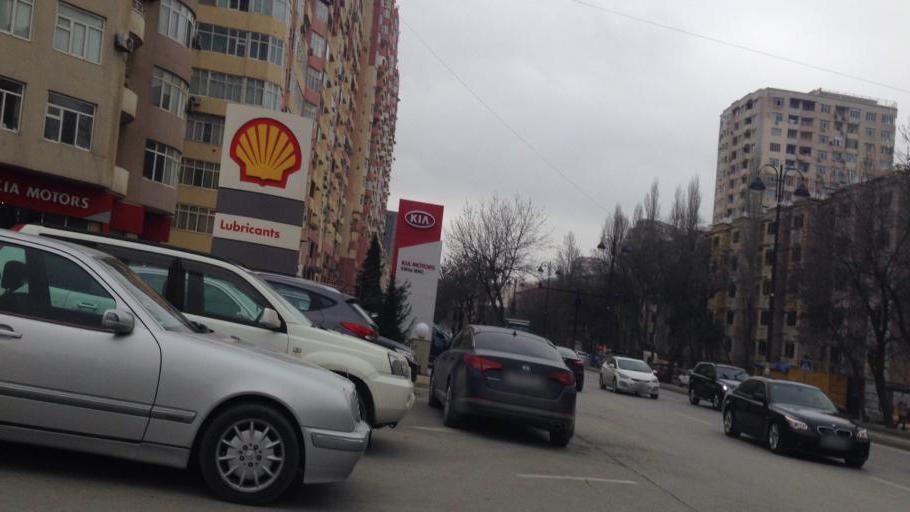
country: AZ
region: Baki
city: Khodzhi-Gasan
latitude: 40.3886
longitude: 49.8079
